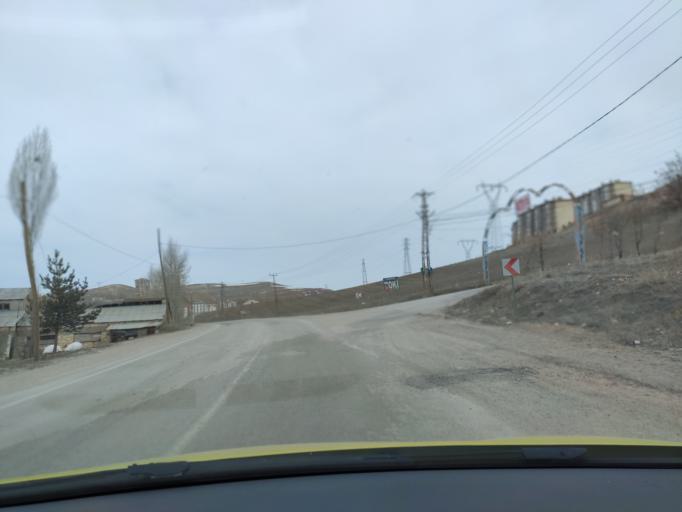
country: TR
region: Bayburt
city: Bayburt
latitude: 40.2632
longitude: 40.2147
